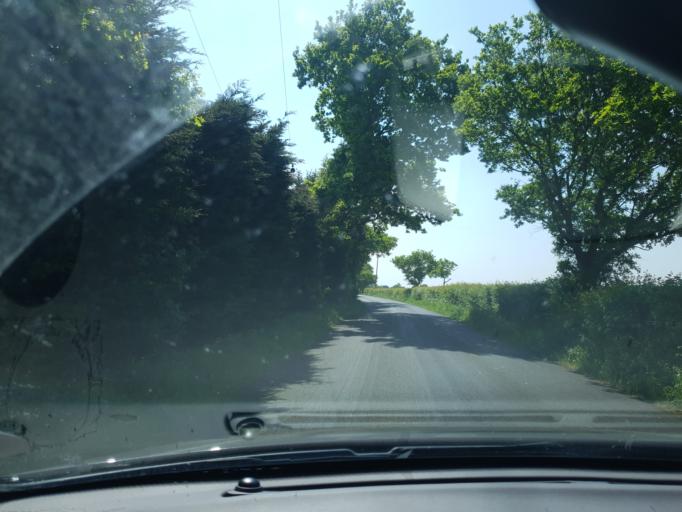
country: GB
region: England
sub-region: Essex
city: Great Bentley
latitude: 51.8580
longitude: 1.0895
